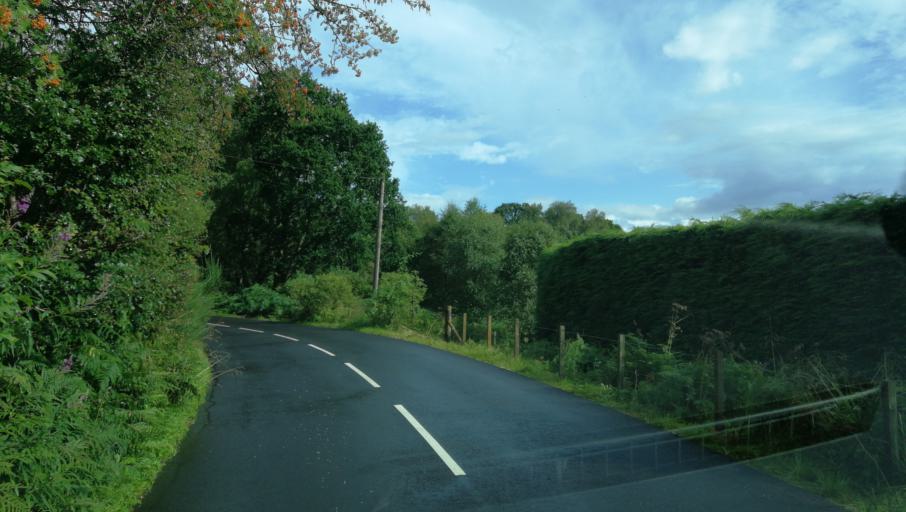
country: GB
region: Scotland
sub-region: Stirling
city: Callander
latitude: 56.2292
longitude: -4.3599
